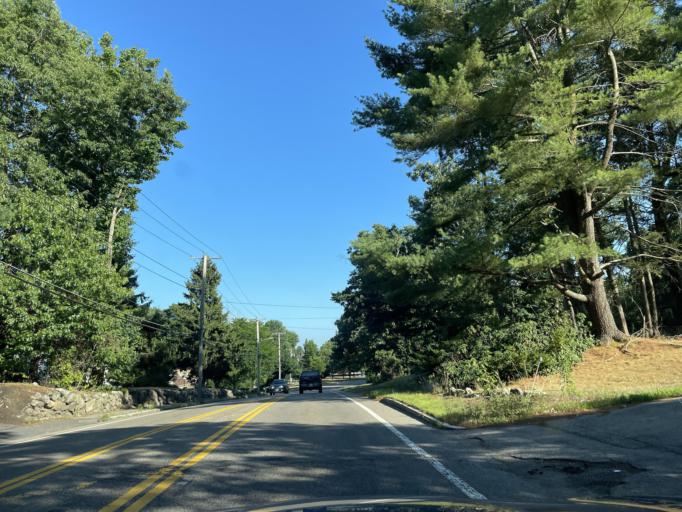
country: US
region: Massachusetts
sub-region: Norfolk County
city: Foxborough
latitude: 42.0575
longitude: -71.2431
